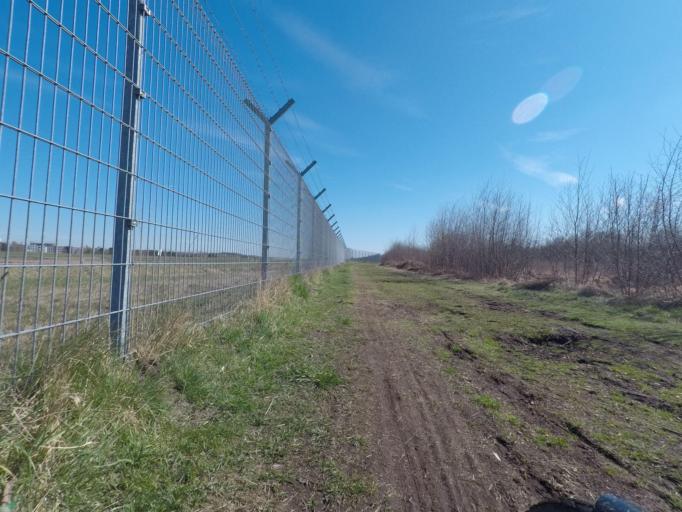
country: DE
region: Hamburg
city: Langenhorn
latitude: 53.6546
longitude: 9.9721
